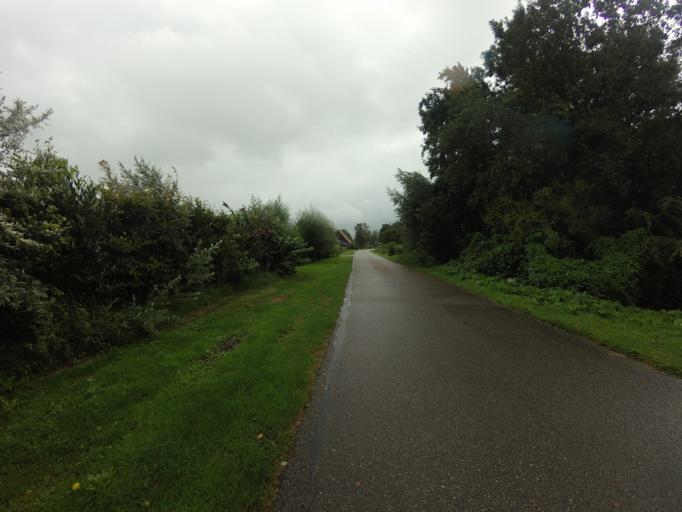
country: NL
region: Overijssel
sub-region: Gemeente Steenwijkerland
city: Blokzijl
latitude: 52.7686
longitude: 5.9871
